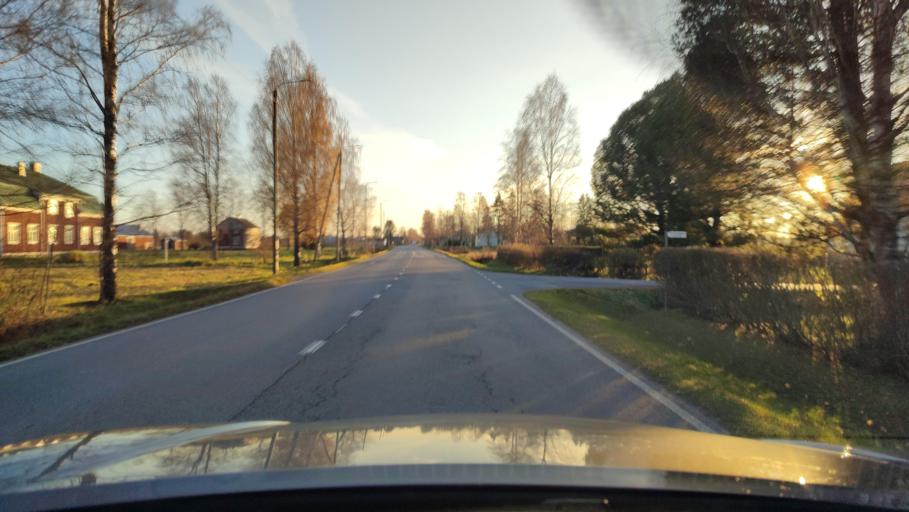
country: FI
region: Ostrobothnia
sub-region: Sydosterbotten
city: Naerpes
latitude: 62.6037
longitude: 21.4579
